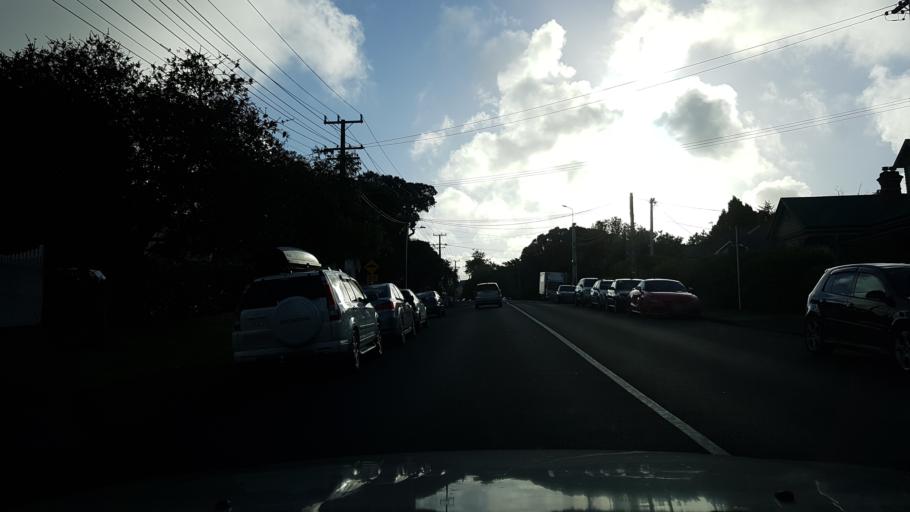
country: NZ
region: Auckland
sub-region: Auckland
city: North Shore
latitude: -36.8174
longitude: 174.7361
